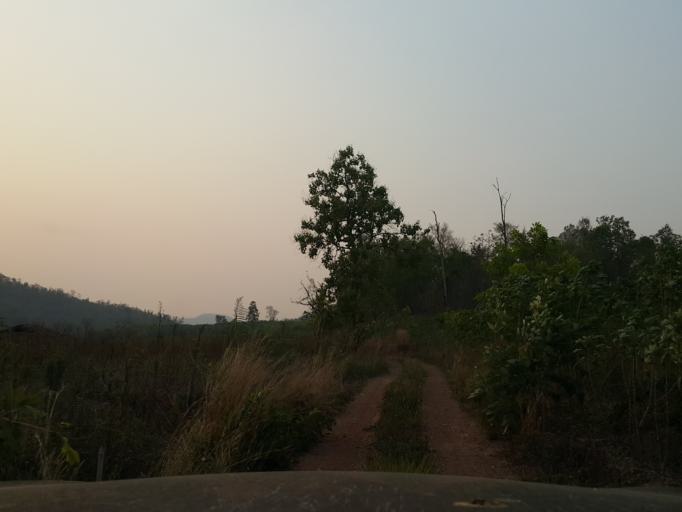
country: TH
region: Lamphun
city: Thung Hua Chang
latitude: 17.9139
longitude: 99.0740
